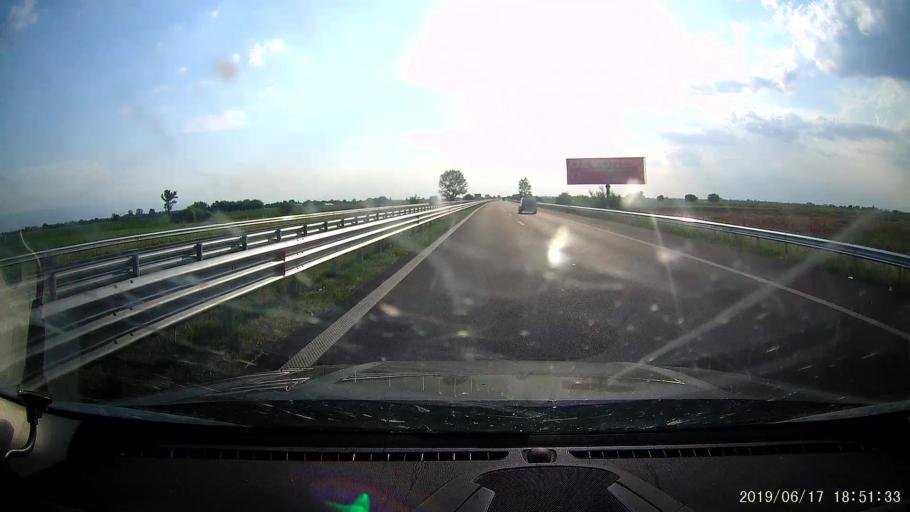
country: BG
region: Plovdiv
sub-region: Obshtina Rakovski
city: Rakovski
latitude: 42.2140
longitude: 24.9680
